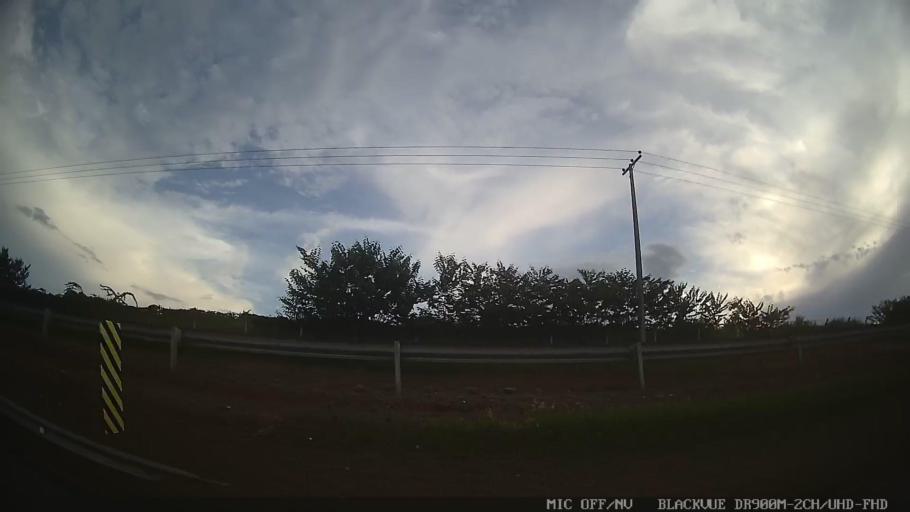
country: BR
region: Sao Paulo
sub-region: Porto Feliz
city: Porto Feliz
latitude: -23.2338
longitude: -47.5156
